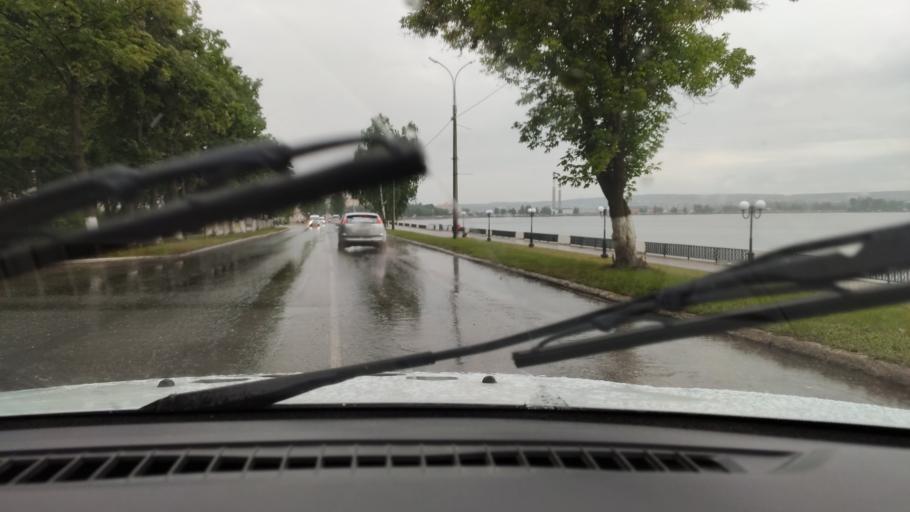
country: RU
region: Udmurtiya
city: Votkinsk
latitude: 57.0613
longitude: 53.9872
